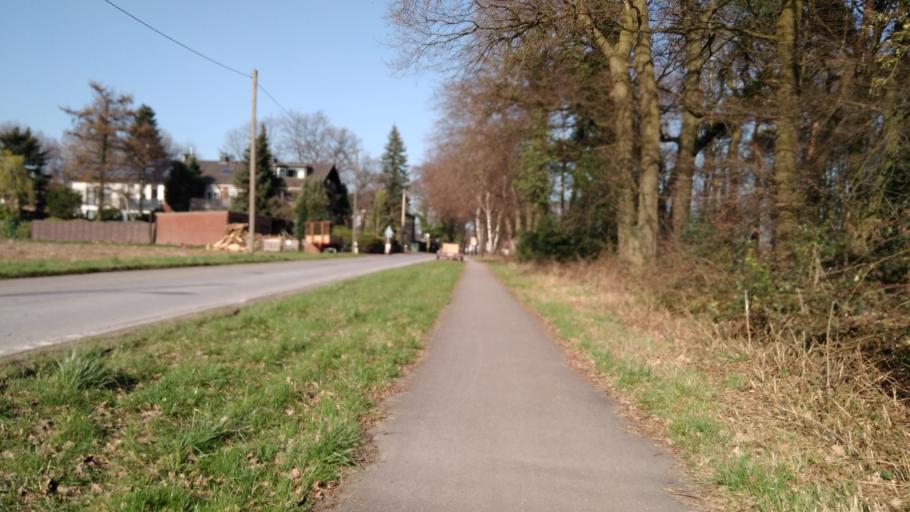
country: DE
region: North Rhine-Westphalia
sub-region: Regierungsbezirk Munster
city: Bottrop
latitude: 51.5724
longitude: 6.8917
